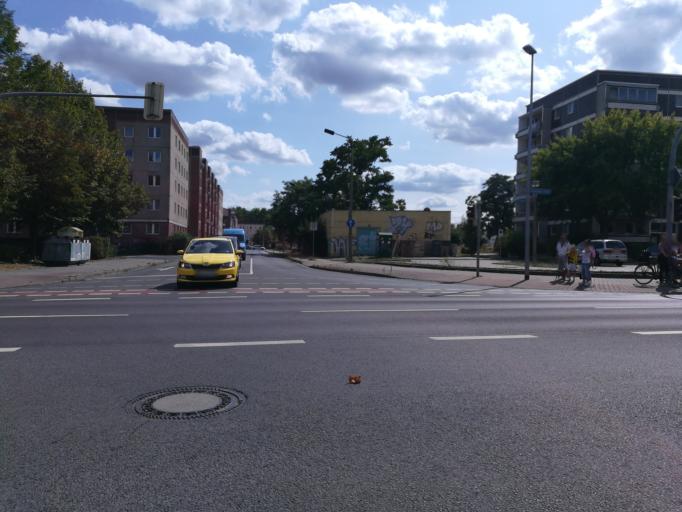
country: DE
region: Saxony-Anhalt
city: Neue Neustadt
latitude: 52.1605
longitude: 11.6310
